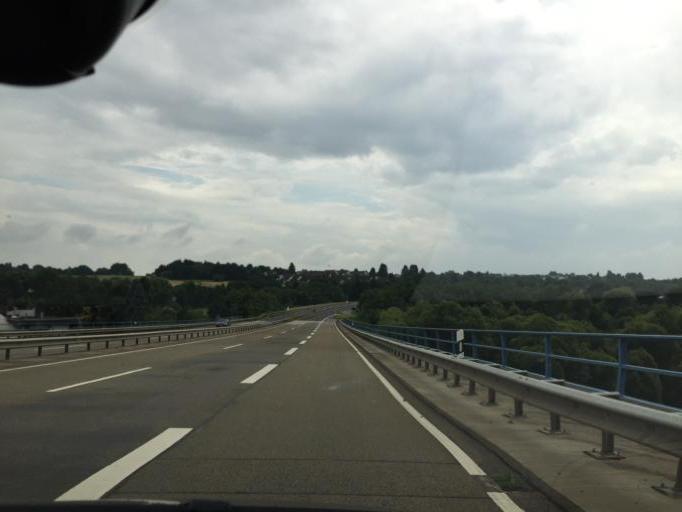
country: DE
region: Rheinland-Pfalz
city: Melsbach
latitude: 50.4690
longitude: 7.4863
